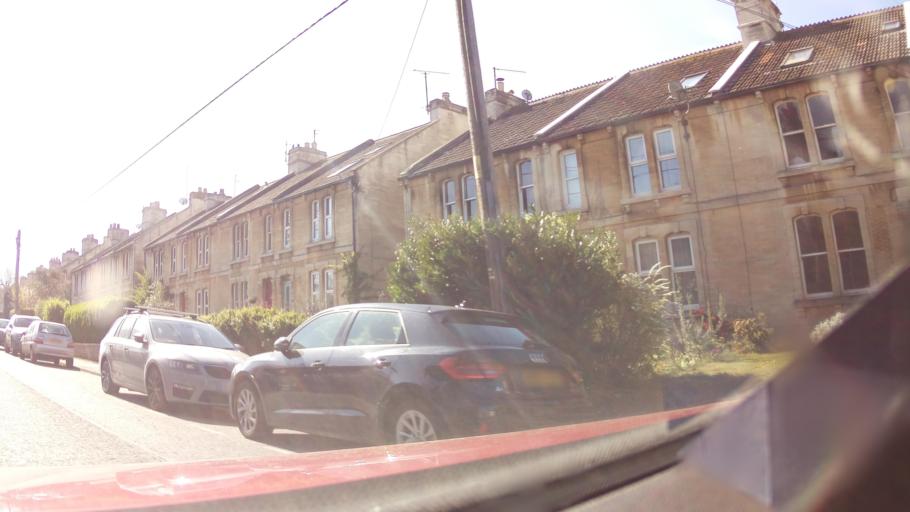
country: GB
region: England
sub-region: Wiltshire
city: Bradford-on-Avon
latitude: 51.3419
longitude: -2.2469
